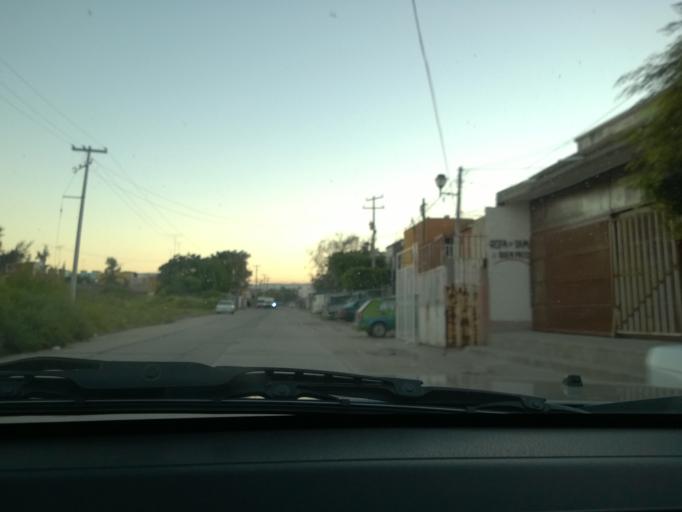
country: MX
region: Guanajuato
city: Leon
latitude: 21.1272
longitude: -101.6549
